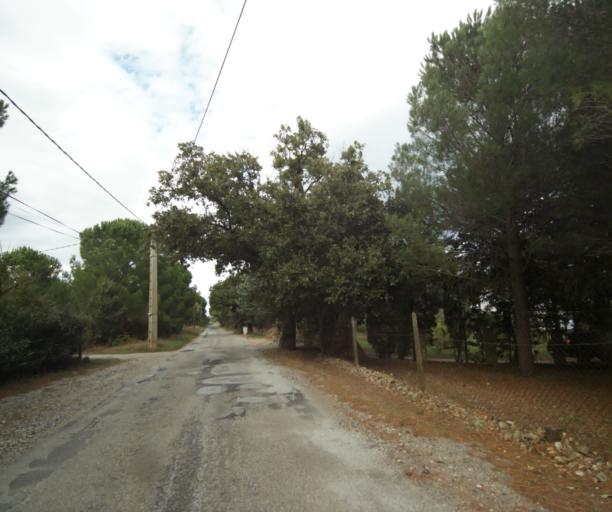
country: FR
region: Languedoc-Roussillon
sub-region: Departement des Pyrenees-Orientales
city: Sant Andreu de Sureda
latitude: 42.5454
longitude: 2.9904
